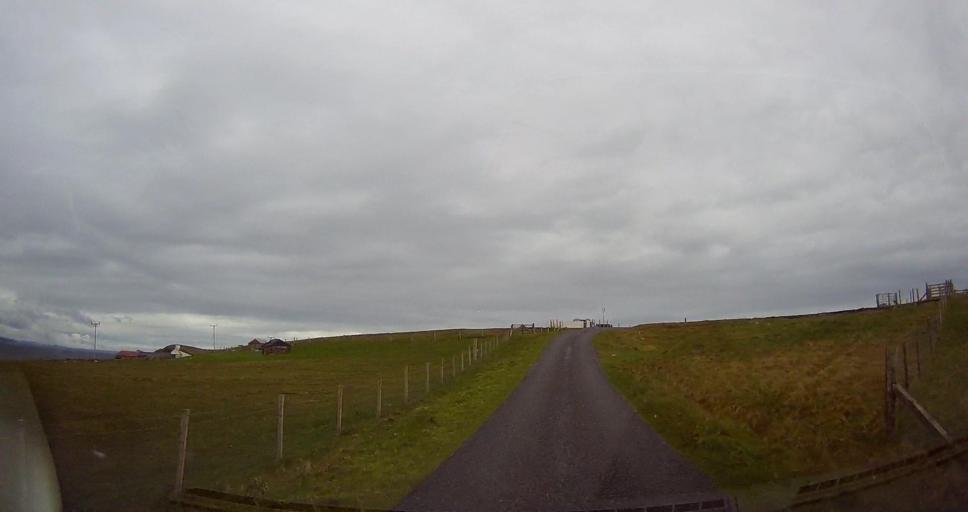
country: GB
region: Scotland
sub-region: Shetland Islands
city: Lerwick
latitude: 60.4817
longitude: -1.6087
